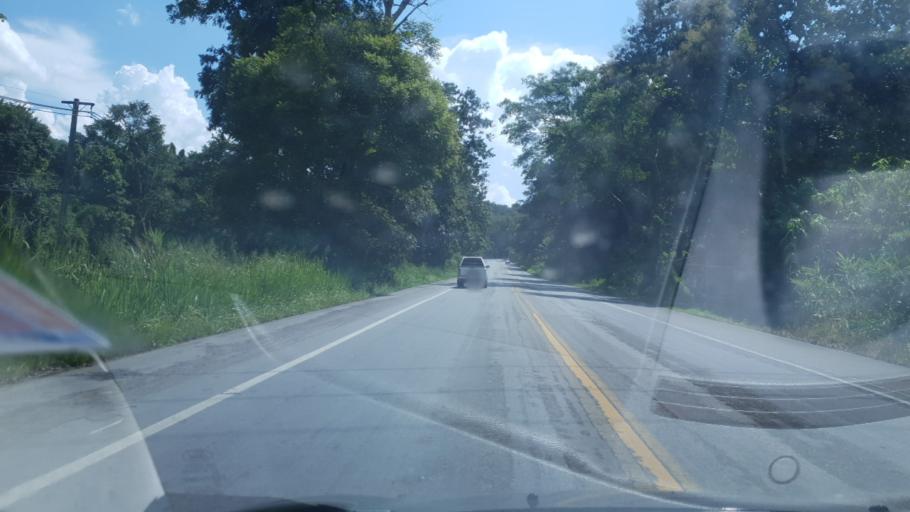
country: TH
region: Chiang Rai
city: Mae Suai
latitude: 19.7037
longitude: 99.5850
